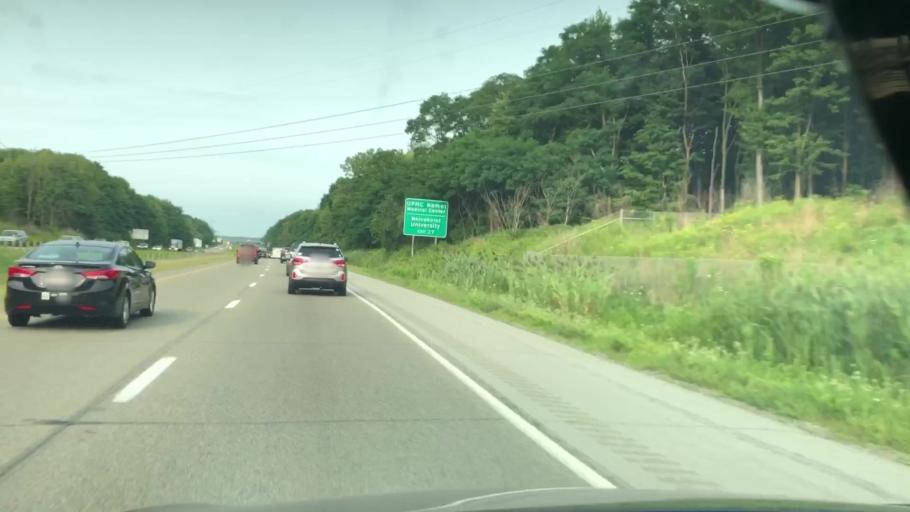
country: US
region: Pennsylvania
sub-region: Erie County
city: Erie
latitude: 42.0540
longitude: -80.0684
